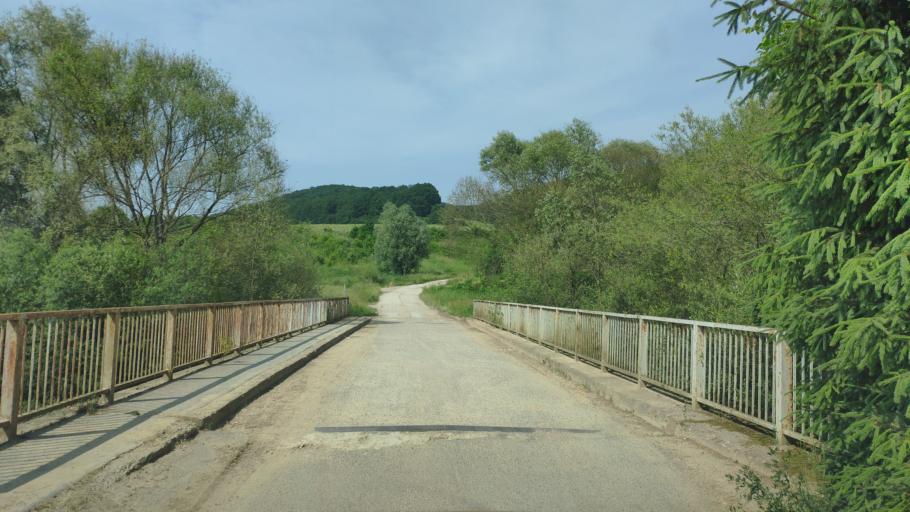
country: SK
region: Presovsky
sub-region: Okres Presov
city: Presov
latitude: 48.9629
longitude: 21.1418
